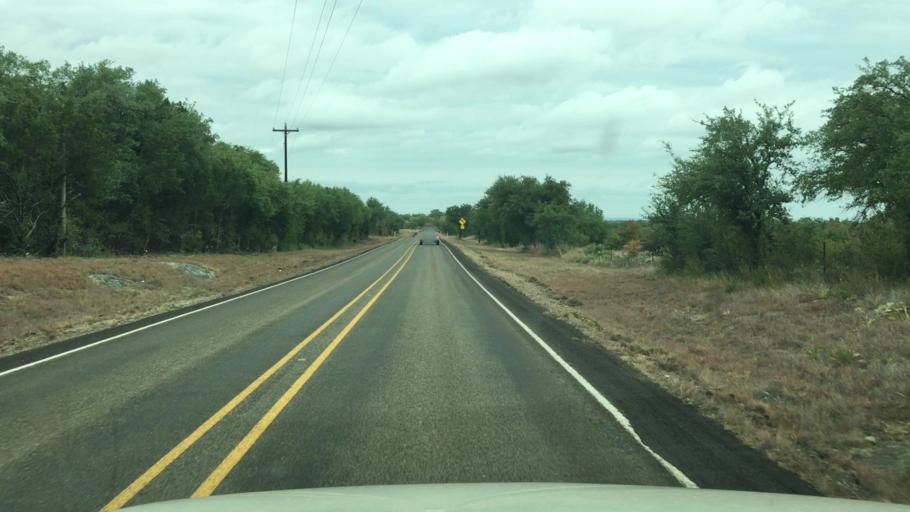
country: US
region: Texas
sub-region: Llano County
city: Horseshoe Bay
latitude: 30.4737
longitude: -98.4159
